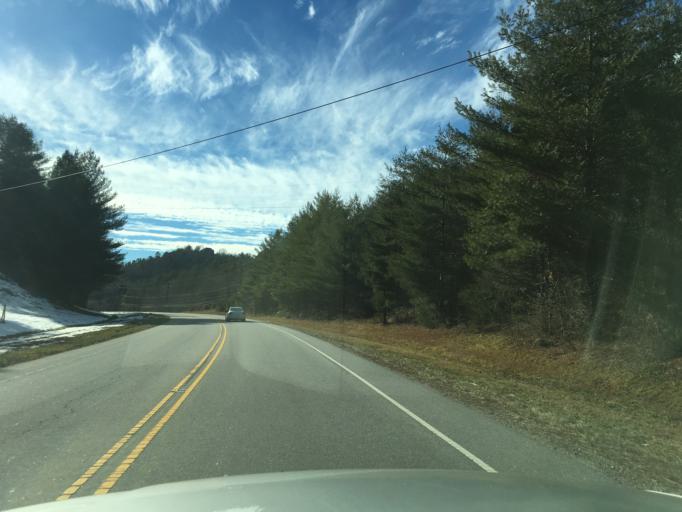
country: US
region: North Carolina
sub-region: Transylvania County
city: Brevard
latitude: 35.1820
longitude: -82.7975
